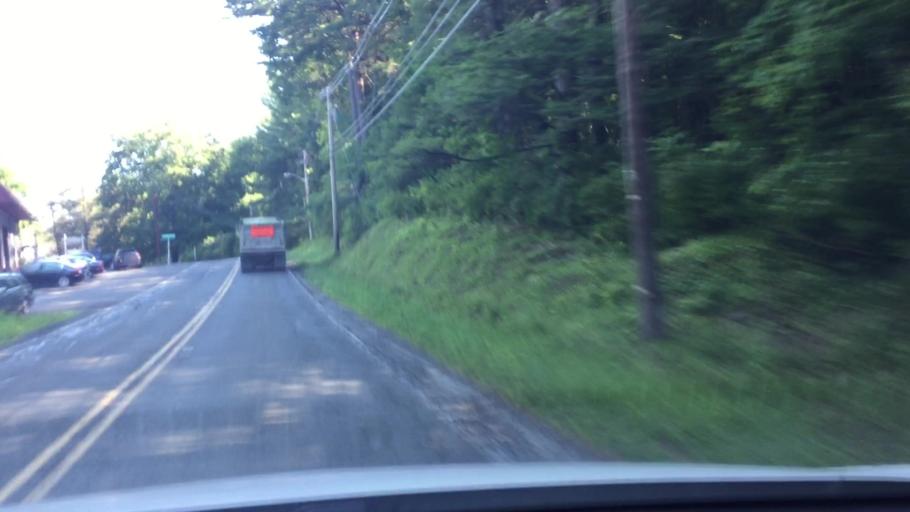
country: US
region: Massachusetts
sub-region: Berkshire County
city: West Stockbridge
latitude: 42.3197
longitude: -73.3681
